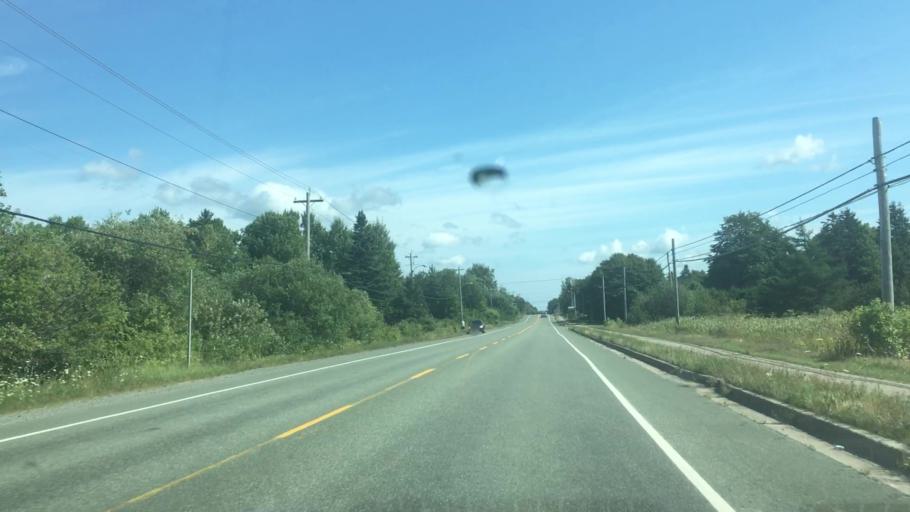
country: CA
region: Nova Scotia
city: Sydney
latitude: 46.0574
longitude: -60.3091
